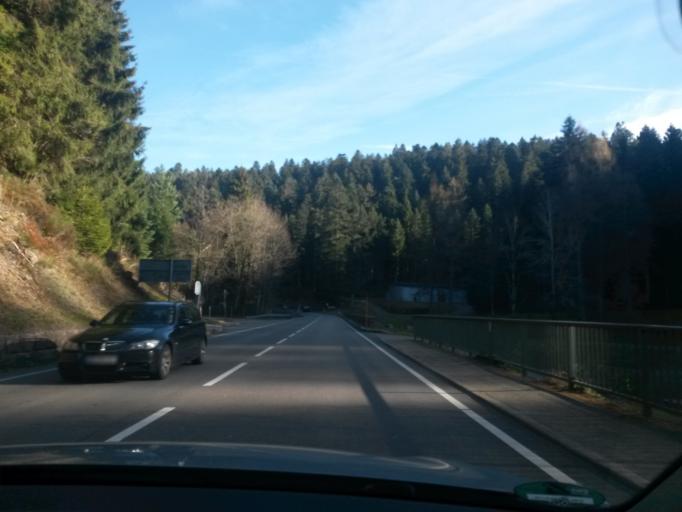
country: DE
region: Baden-Wuerttemberg
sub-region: Karlsruhe Region
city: Freudenstadt
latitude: 48.4514
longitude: 8.3940
